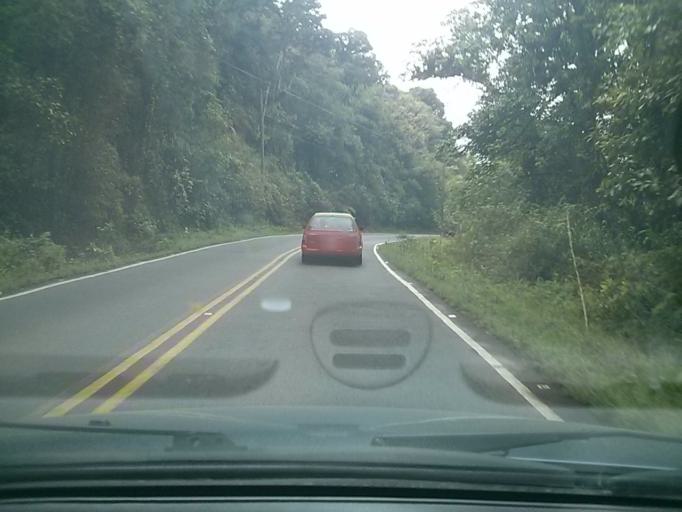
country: CR
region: San Jose
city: San Marcos
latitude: 9.7418
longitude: -83.9686
